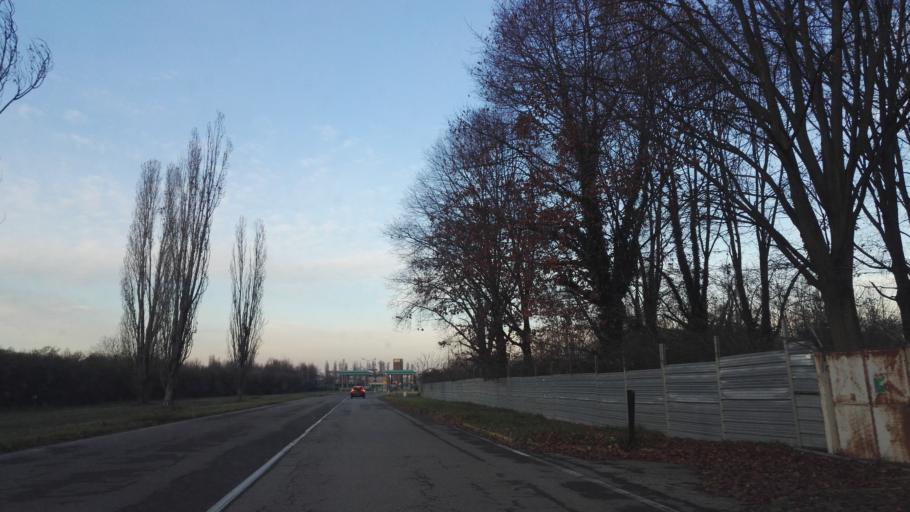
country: IT
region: Lombardy
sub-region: Citta metropolitana di Milano
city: Novegro-Tregarezzo-San Felice
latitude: 45.4685
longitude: 9.2971
